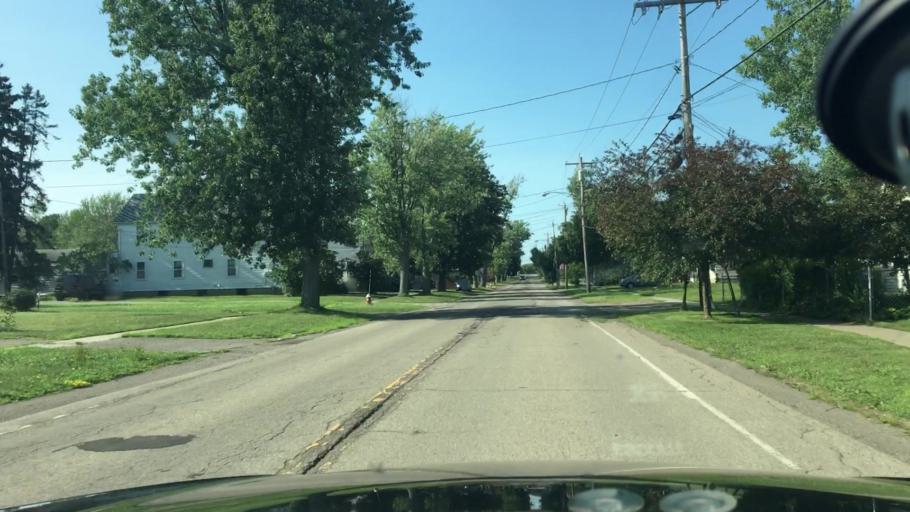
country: US
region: New York
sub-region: Erie County
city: Angola
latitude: 42.6331
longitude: -79.0277
